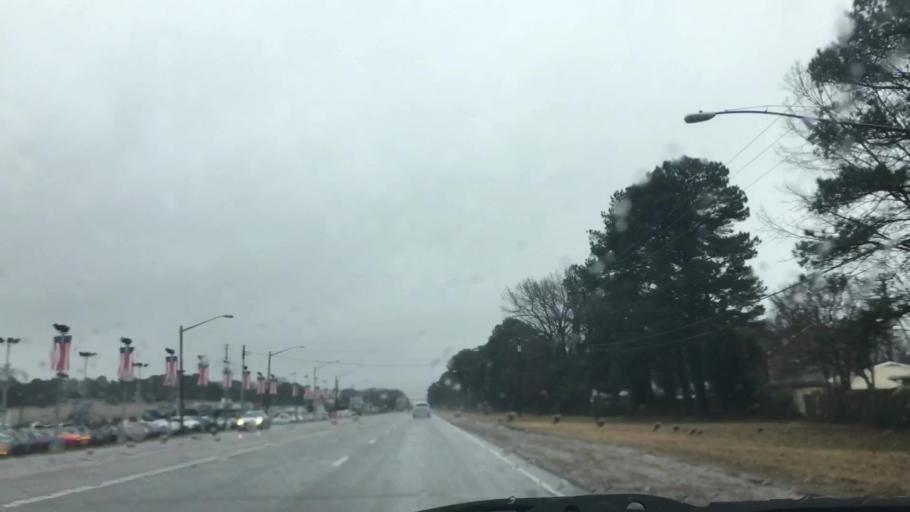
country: US
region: Virginia
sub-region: City of Norfolk
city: Norfolk
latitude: 36.9128
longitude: -76.2368
